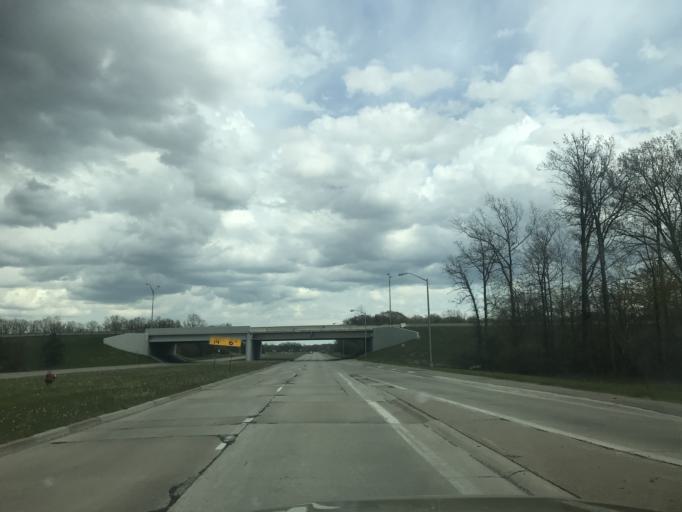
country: US
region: Michigan
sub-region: Wayne County
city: Romulus
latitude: 42.1927
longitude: -83.3670
